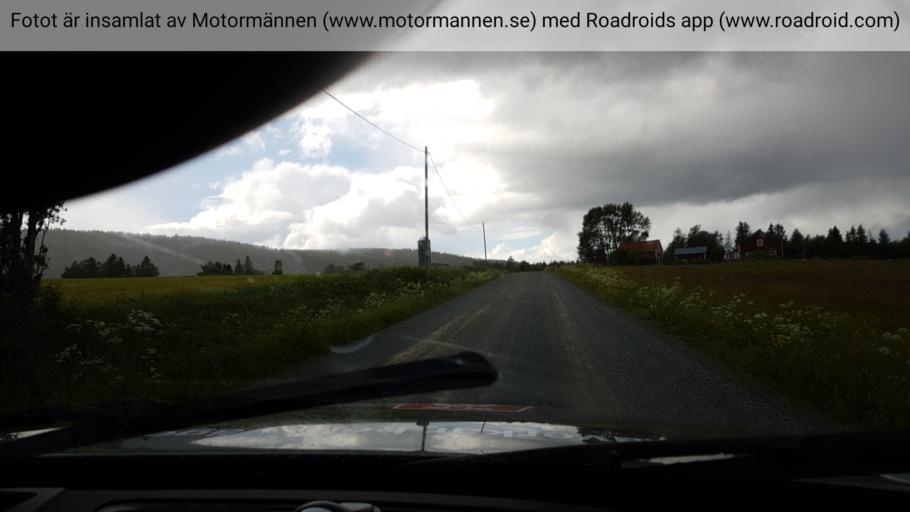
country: SE
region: Jaemtland
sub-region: Bergs Kommun
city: Hoverberg
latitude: 62.9602
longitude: 14.2421
